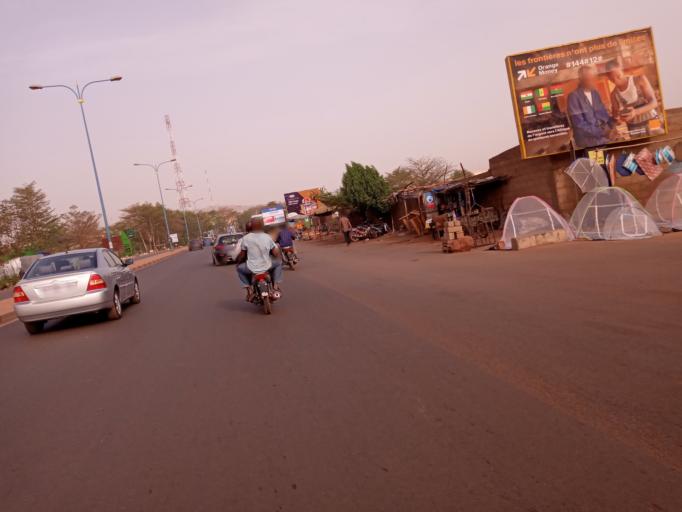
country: ML
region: Bamako
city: Bamako
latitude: 12.6377
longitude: -8.0177
